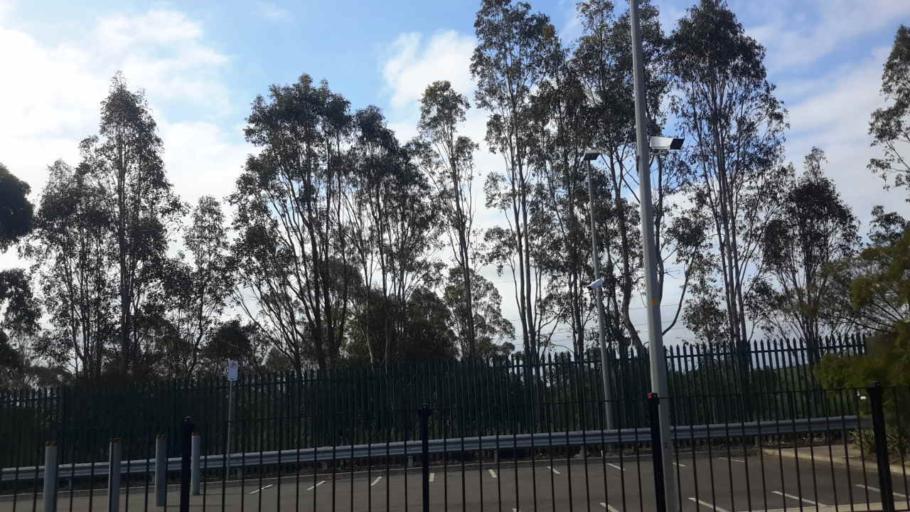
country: AU
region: New South Wales
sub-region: Campbelltown Municipality
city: Glen Alpine
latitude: -34.0729
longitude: 150.7947
